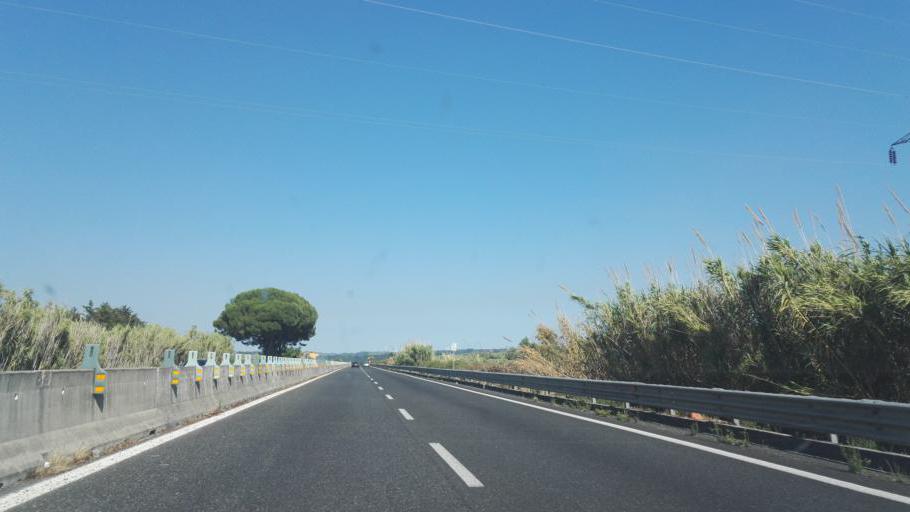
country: IT
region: Calabria
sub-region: Provincia di Catanzaro
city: Santa Eufemia Lamezia
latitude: 38.9134
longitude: 16.2945
